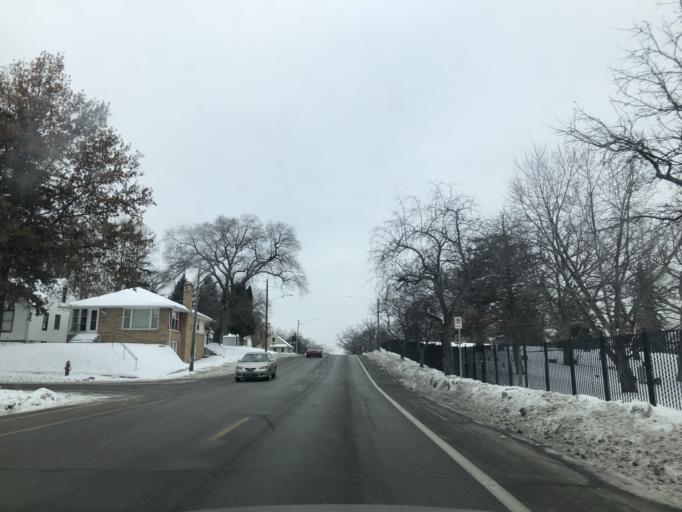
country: US
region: Minnesota
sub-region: Hennepin County
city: Robbinsdale
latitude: 45.0241
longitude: -93.3016
